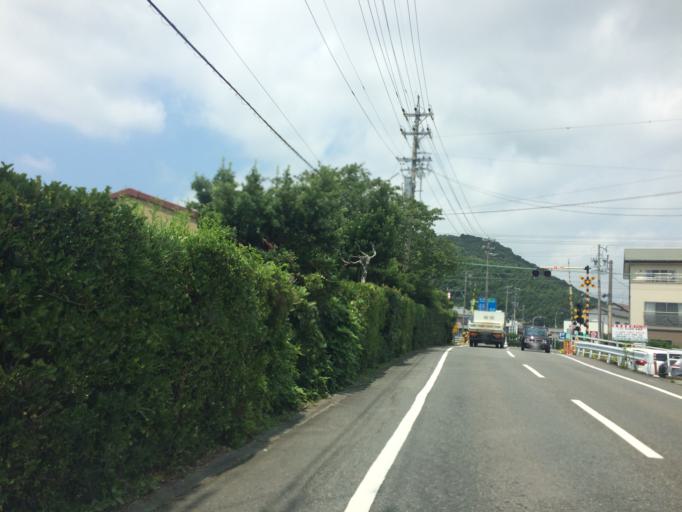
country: JP
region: Shizuoka
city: Shimada
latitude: 34.8351
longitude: 138.2007
